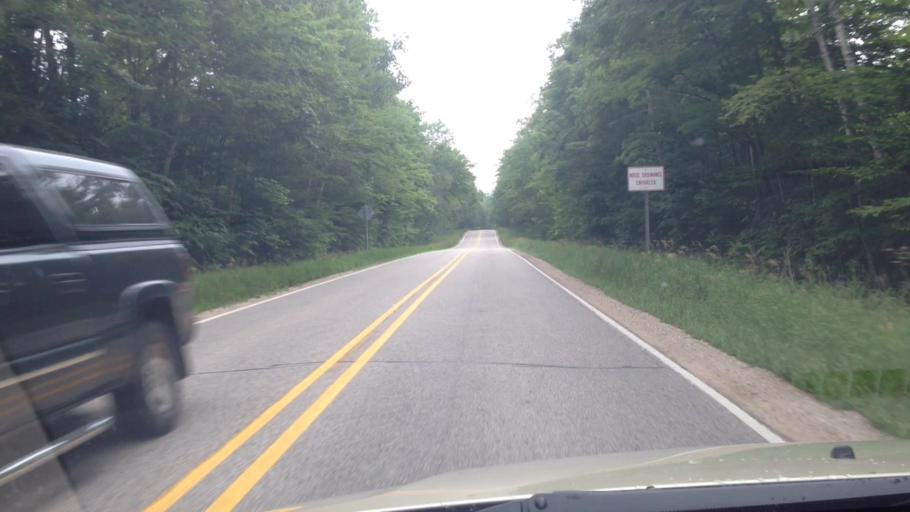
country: US
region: Michigan
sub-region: Mackinac County
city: Saint Ignace
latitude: 46.0408
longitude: -85.1129
